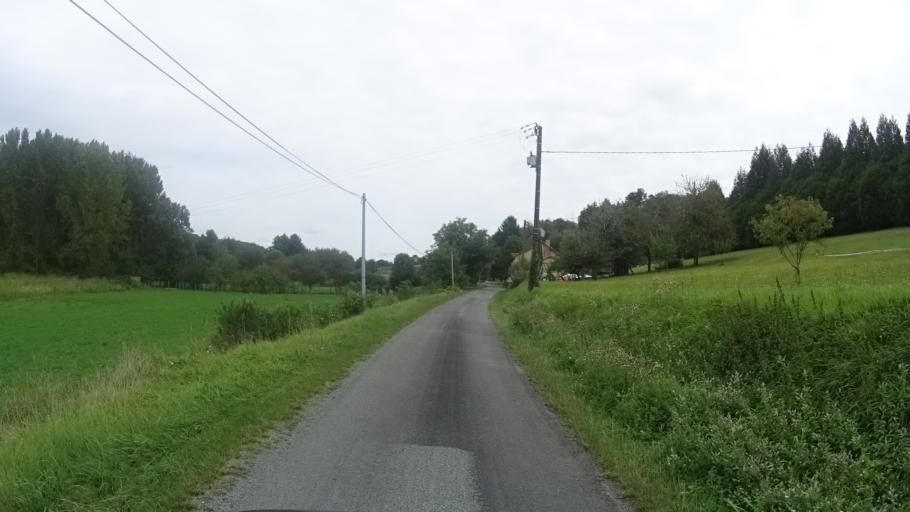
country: FR
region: Aquitaine
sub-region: Departement de la Dordogne
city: Neuvic
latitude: 45.0229
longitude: 0.4979
